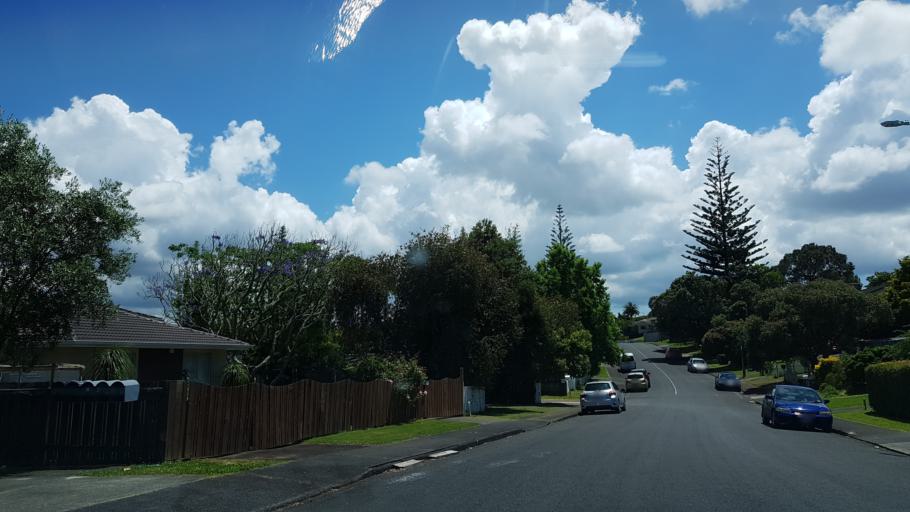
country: NZ
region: Auckland
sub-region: Auckland
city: North Shore
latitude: -36.7916
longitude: 174.6985
